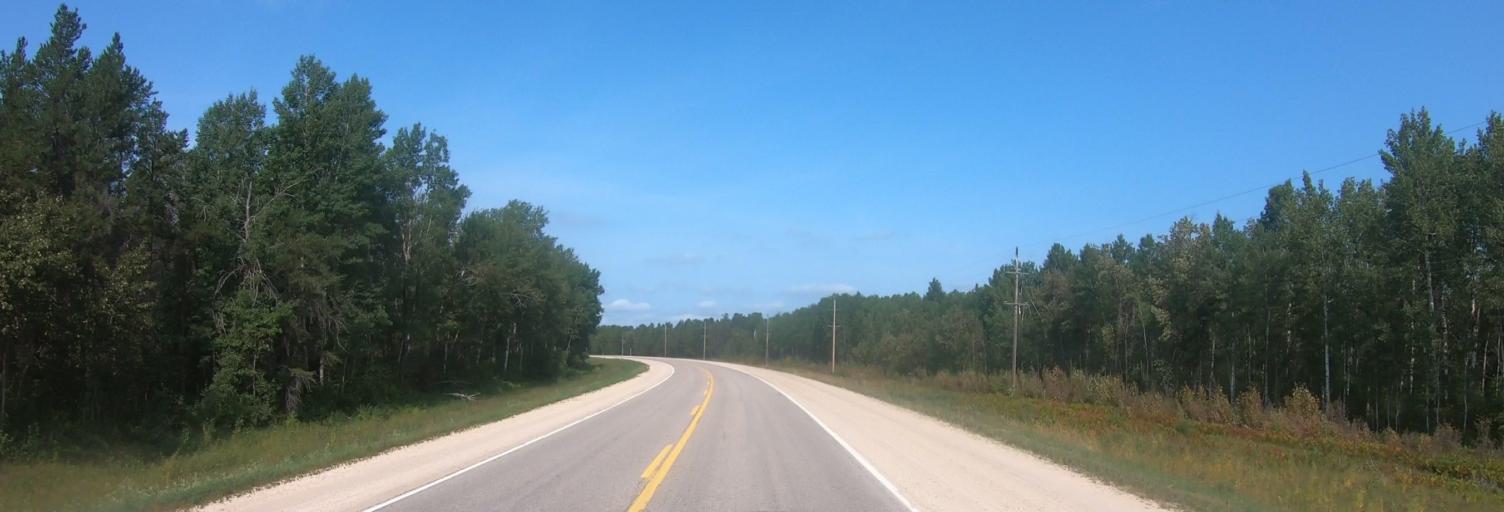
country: CA
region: Manitoba
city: La Broquerie
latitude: 49.1732
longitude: -96.1603
